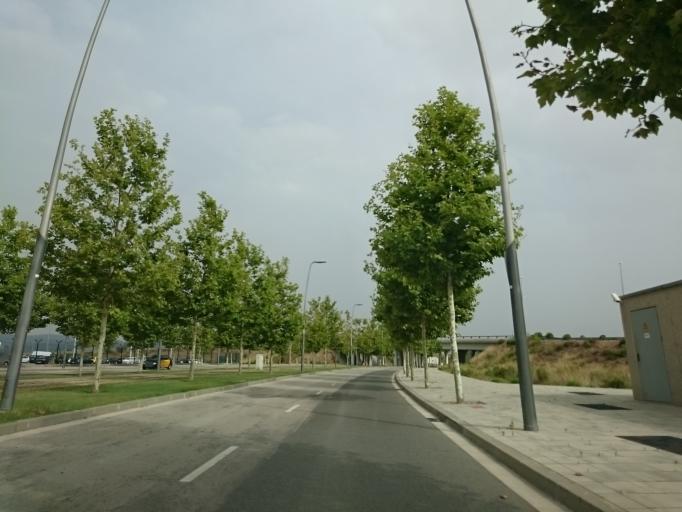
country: ES
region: Catalonia
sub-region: Provincia de Barcelona
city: Viladecans
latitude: 41.2933
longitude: 2.0531
